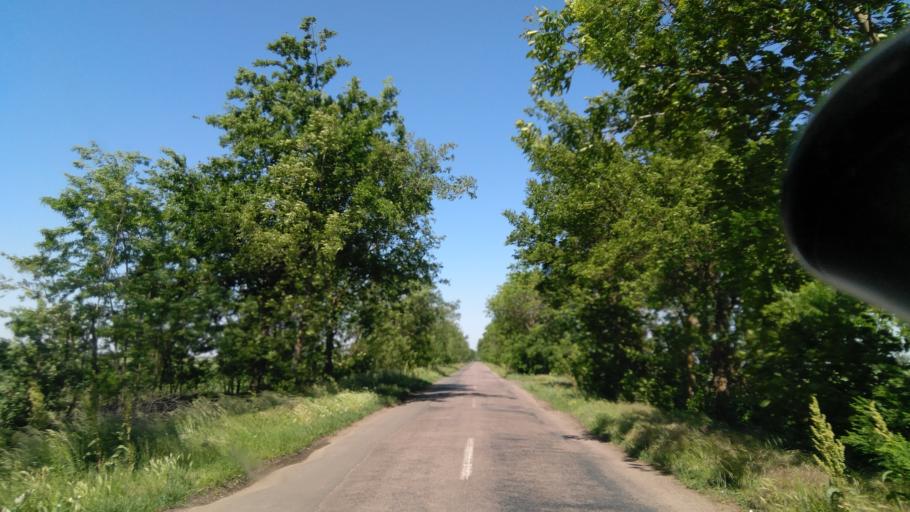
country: HU
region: Bekes
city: Kunagota
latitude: 46.4242
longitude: 21.1036
